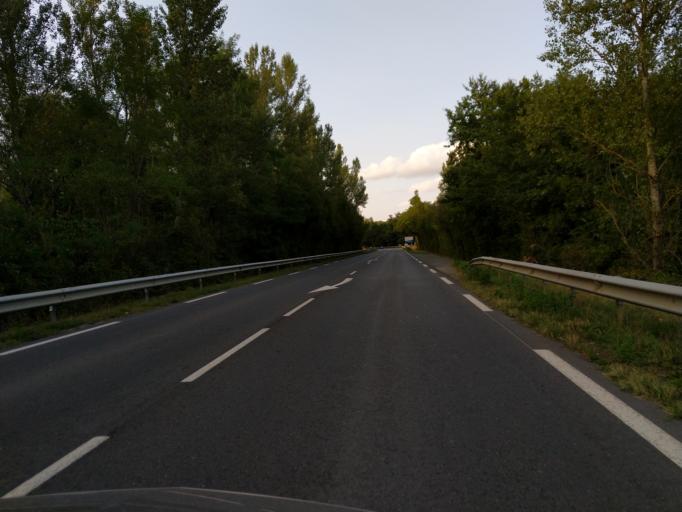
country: FR
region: Midi-Pyrenees
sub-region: Departement du Tarn
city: Realmont
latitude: 43.7854
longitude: 2.1879
